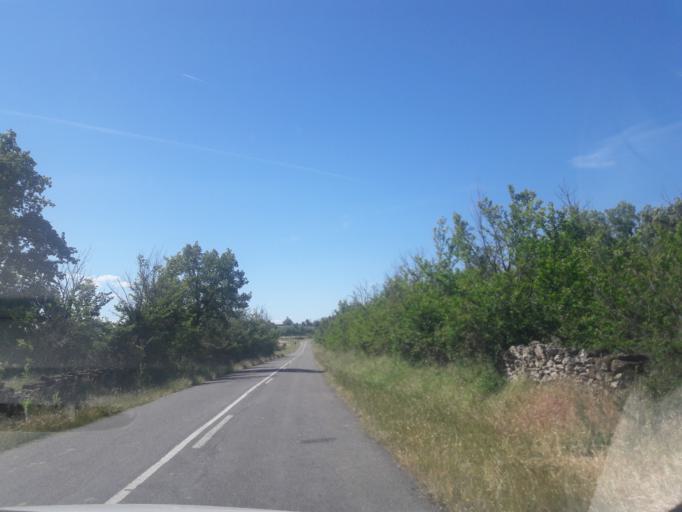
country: ES
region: Castille and Leon
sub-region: Provincia de Salamanca
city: Lumbrales
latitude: 40.9482
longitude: -6.7167
